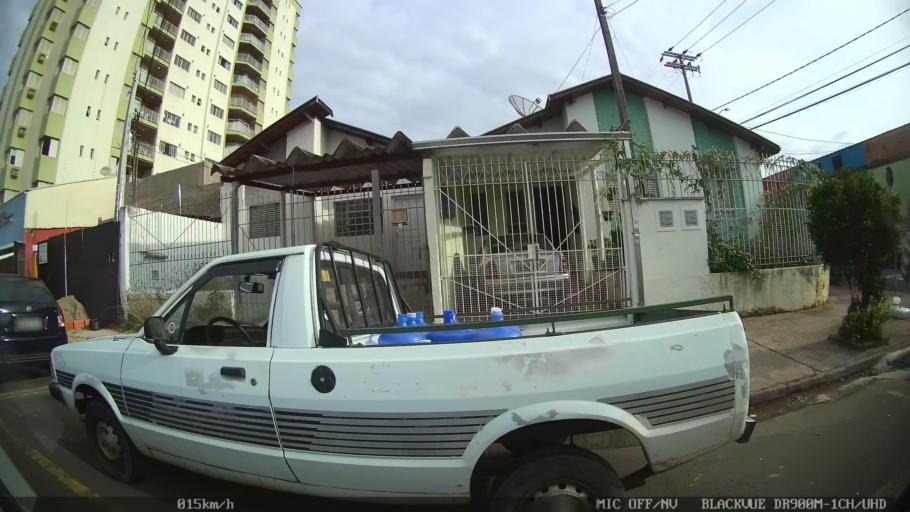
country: BR
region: Sao Paulo
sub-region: Piracicaba
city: Piracicaba
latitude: -22.7286
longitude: -47.6321
